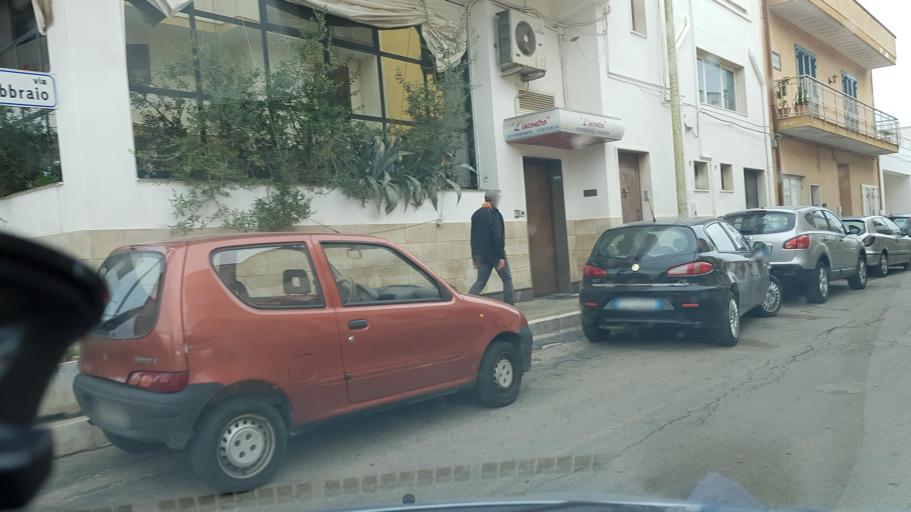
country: IT
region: Apulia
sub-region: Provincia di Lecce
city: Veglie
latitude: 40.3338
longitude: 17.9605
